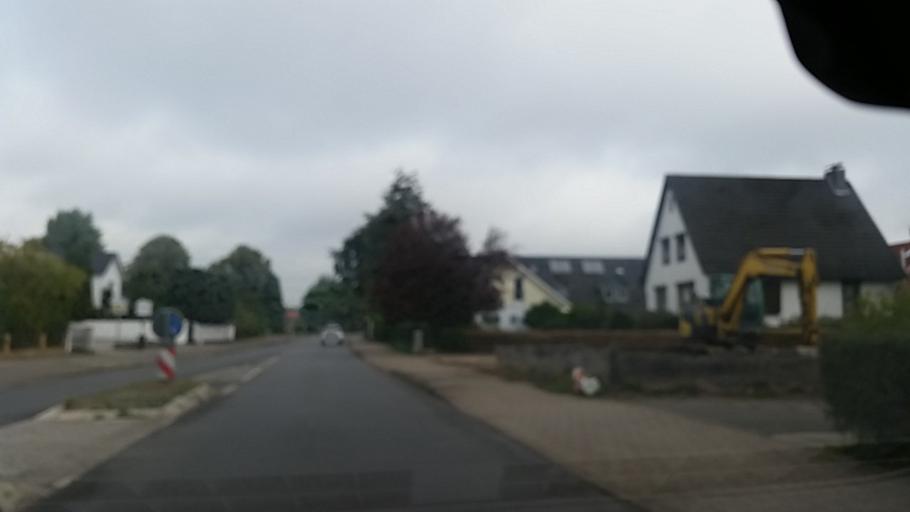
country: DE
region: Schleswig-Holstein
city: Henstedt-Ulzburg
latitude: 53.7723
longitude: 9.9788
